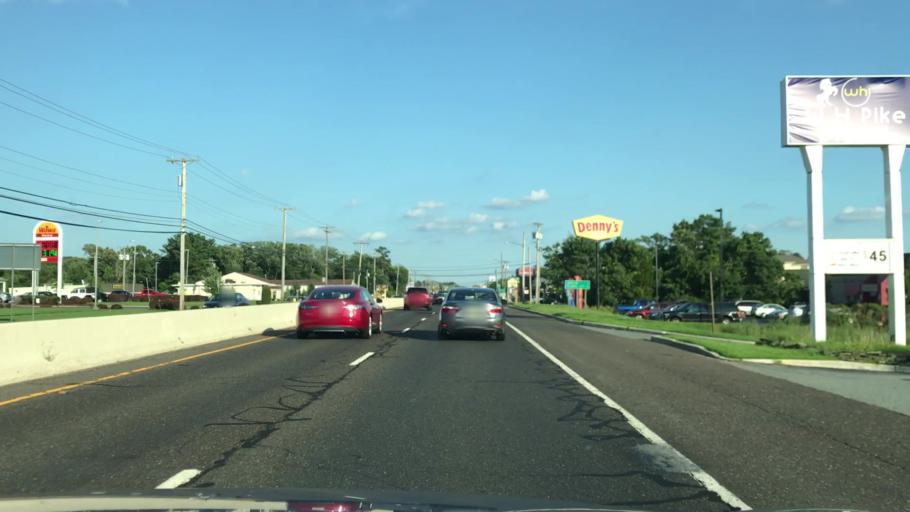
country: US
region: New Jersey
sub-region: Atlantic County
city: Absecon
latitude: 39.4470
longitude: -74.5299
